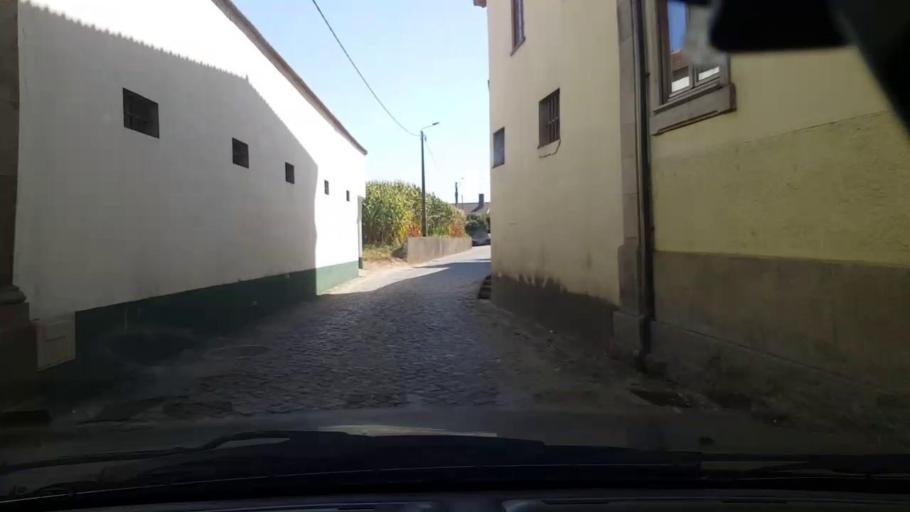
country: PT
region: Porto
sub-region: Matosinhos
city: Lavra
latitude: 41.2916
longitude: -8.6900
